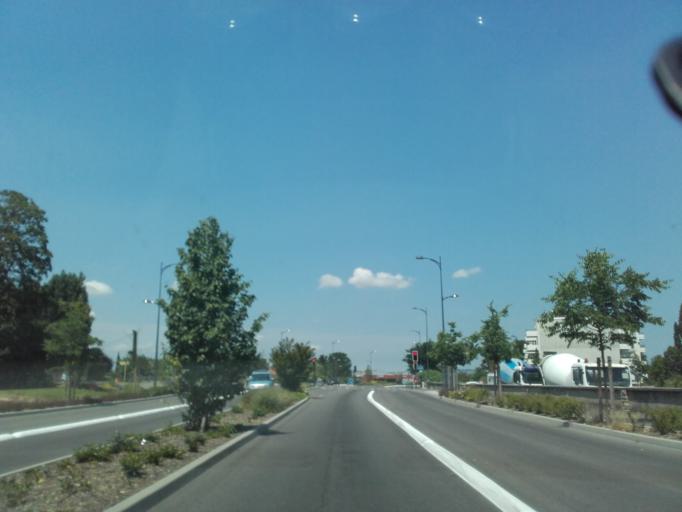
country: FR
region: Rhone-Alpes
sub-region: Departement de l'Isere
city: Bourgoin-Jallieu
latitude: 45.5901
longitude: 5.2727
